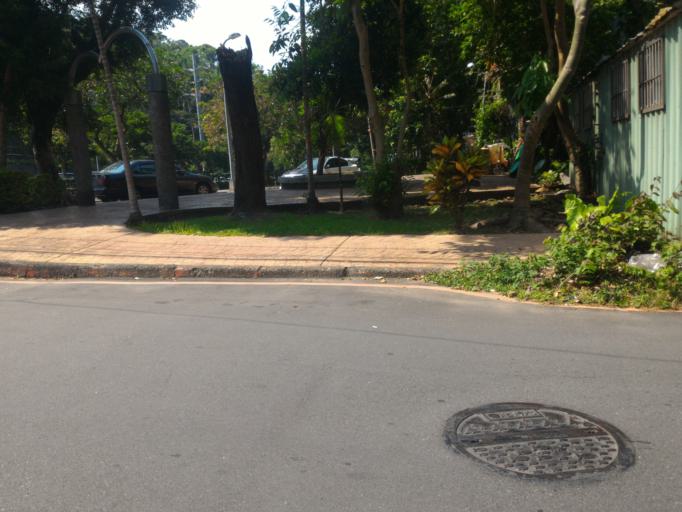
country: TW
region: Taipei
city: Taipei
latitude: 25.0372
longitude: 121.6168
